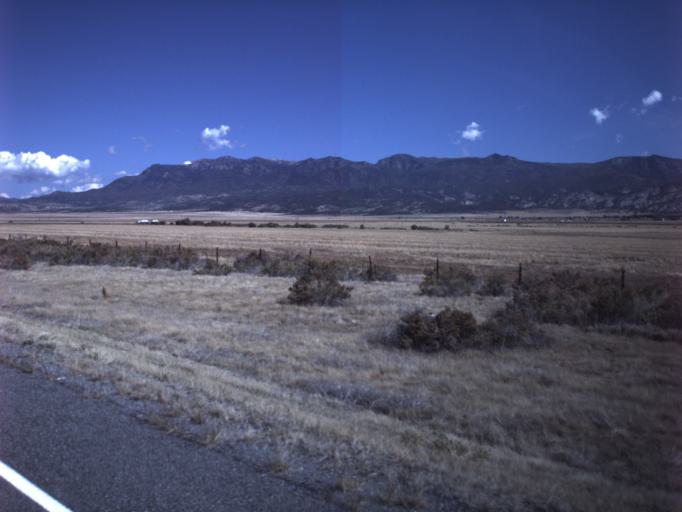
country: US
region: Utah
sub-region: Juab County
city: Nephi
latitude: 39.5523
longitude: -111.9226
